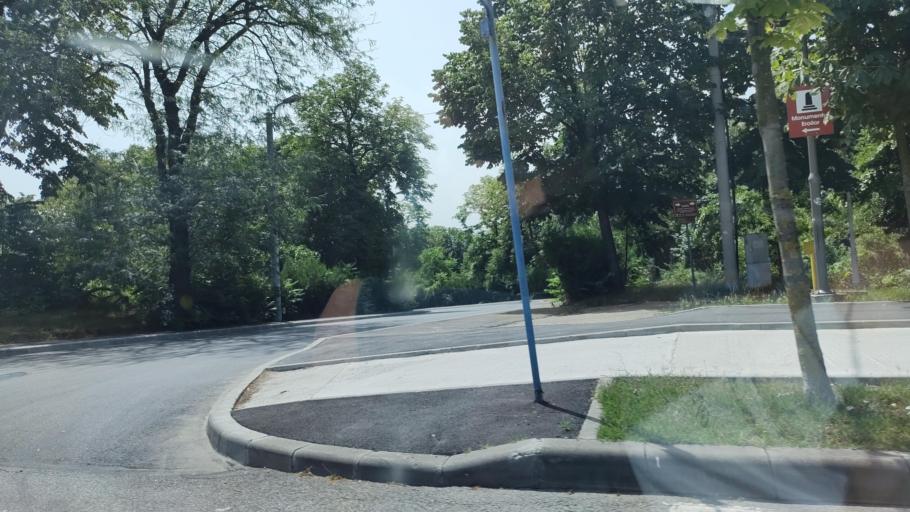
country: RO
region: Mehedinti
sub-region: Municipiul Drobeta-Turnu Severin
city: Drobeta-Turnu Severin
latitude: 44.6231
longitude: 22.6473
